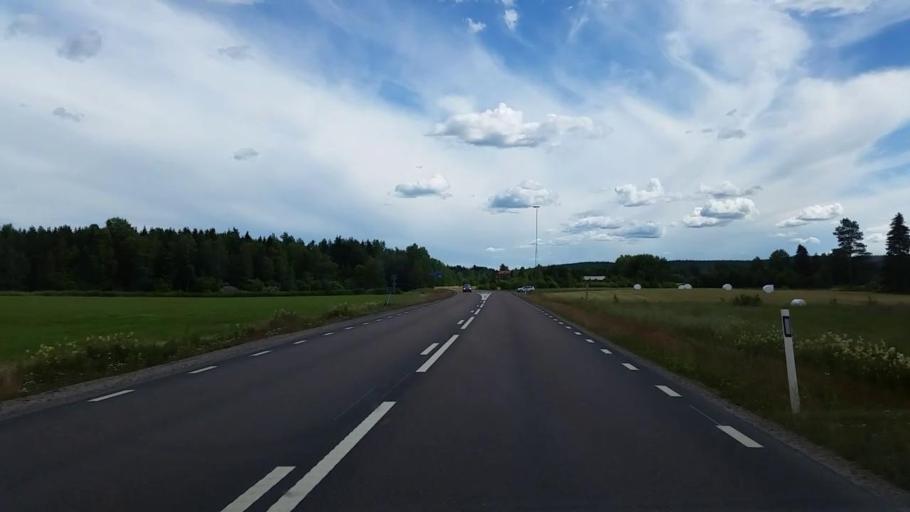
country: SE
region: Gaevleborg
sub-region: Ovanakers Kommun
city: Edsbyn
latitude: 61.3729
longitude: 15.8466
